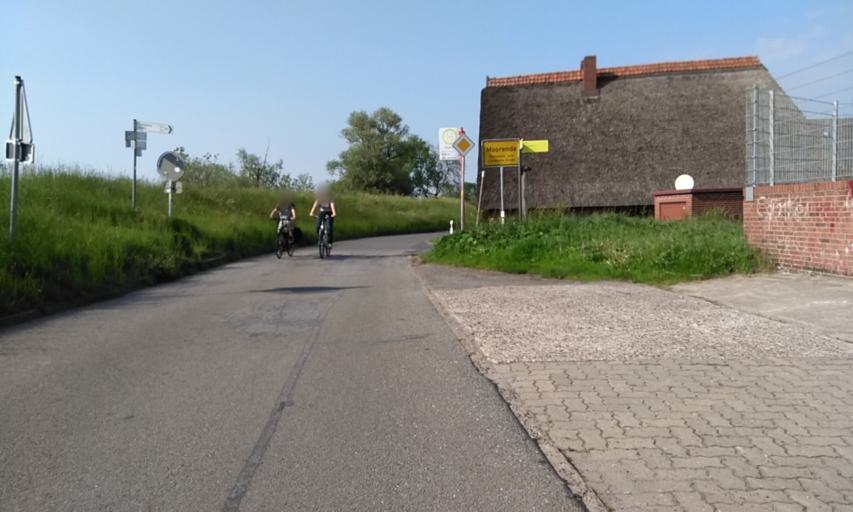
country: DE
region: Lower Saxony
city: Buxtehude
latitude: 53.4924
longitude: 9.7164
